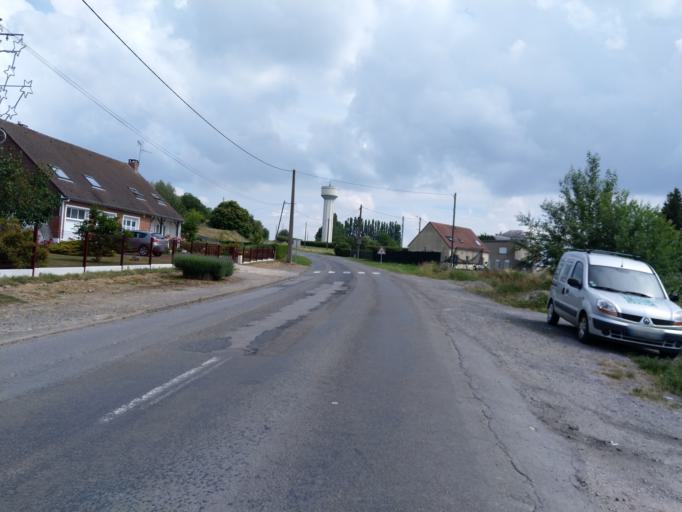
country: FR
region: Nord-Pas-de-Calais
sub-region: Departement du Nord
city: Boussois
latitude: 50.3240
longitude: 4.0073
